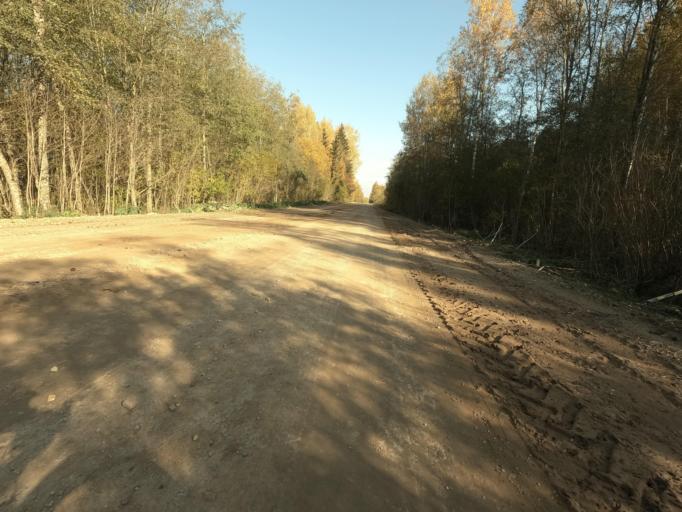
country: RU
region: Novgorod
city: Batetskiy
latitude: 58.8281
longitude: 30.7116
